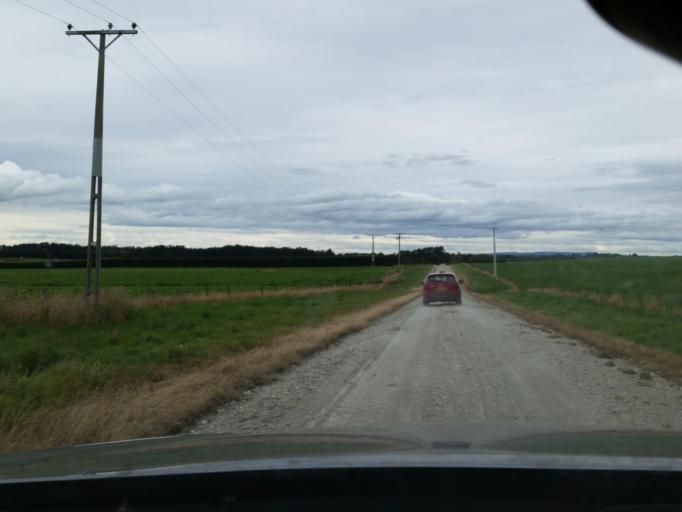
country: NZ
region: Southland
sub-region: Invercargill City
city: Invercargill
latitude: -46.3895
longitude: 168.5776
